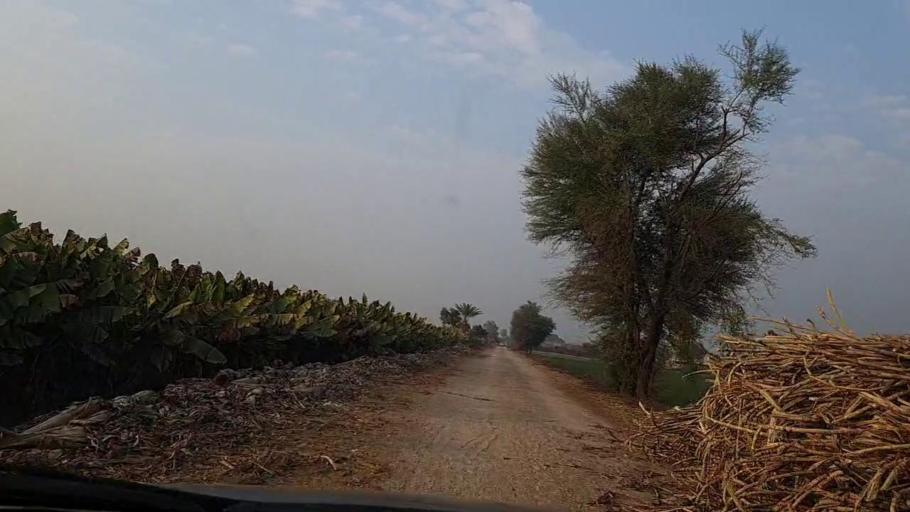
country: PK
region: Sindh
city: Nawabshah
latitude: 26.2907
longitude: 68.2854
